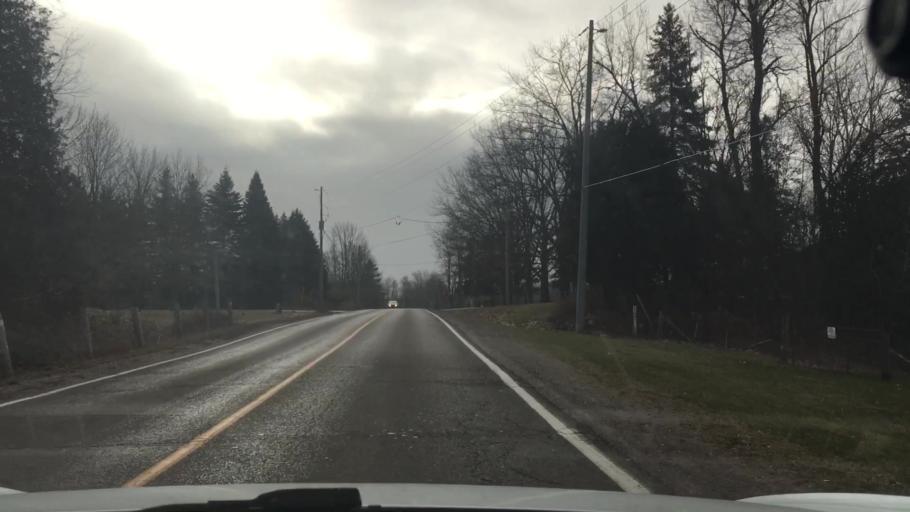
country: CA
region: Ontario
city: Oshawa
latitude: 43.9344
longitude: -78.7987
